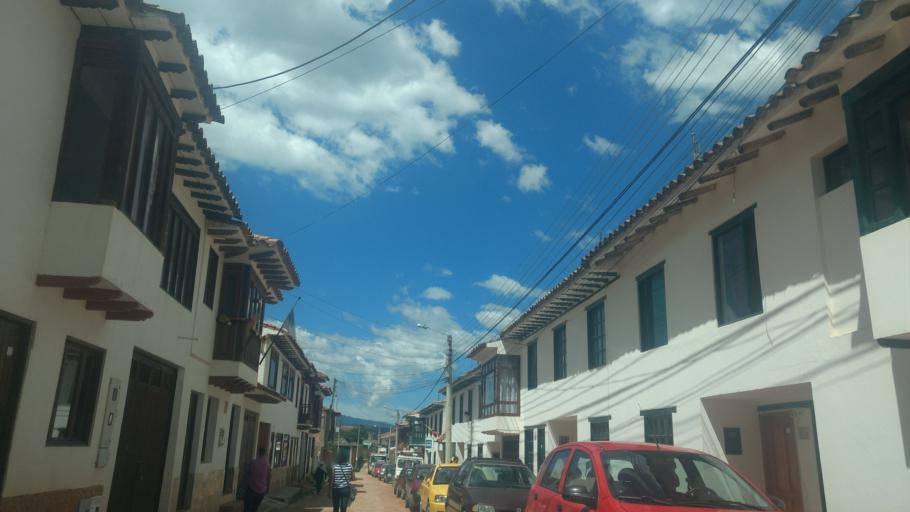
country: CO
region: Boyaca
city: Villa de Leiva
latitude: 5.6286
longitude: -73.5260
